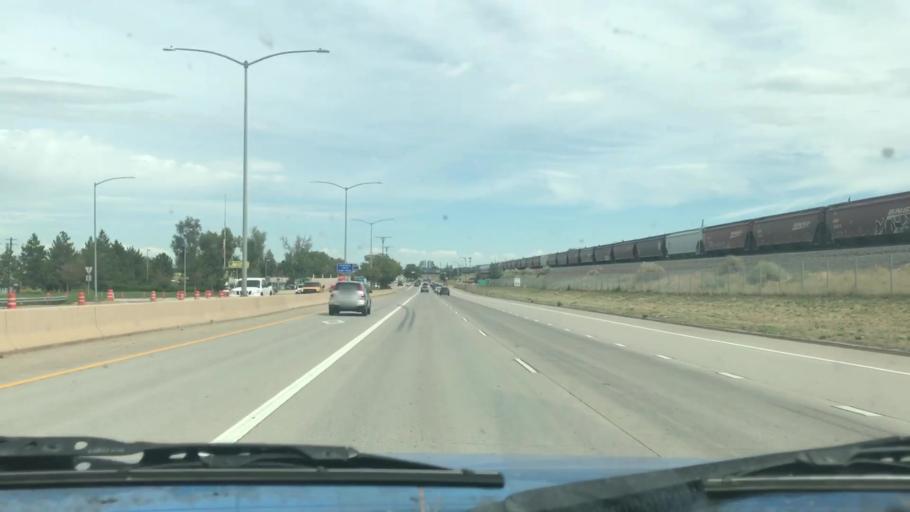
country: US
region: Colorado
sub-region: Arapahoe County
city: Englewood
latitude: 39.6565
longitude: -105.0003
